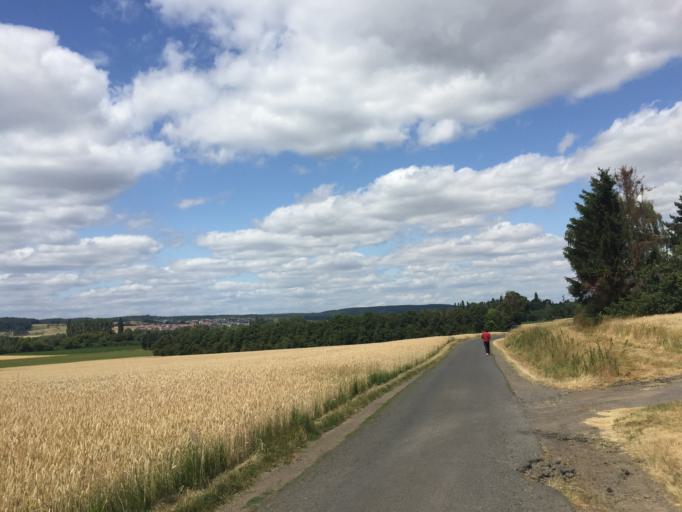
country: DE
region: Hesse
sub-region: Regierungsbezirk Giessen
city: Giessen
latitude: 50.6132
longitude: 8.6920
